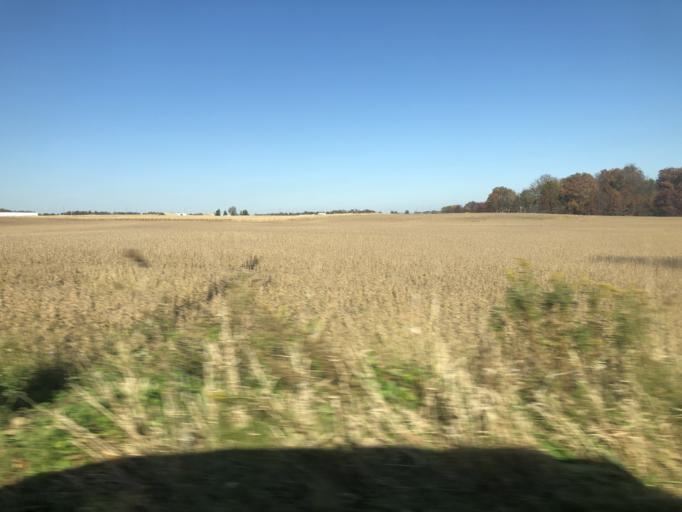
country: US
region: Indiana
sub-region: Allen County
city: Fort Wayne
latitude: 41.1102
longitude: -85.2206
